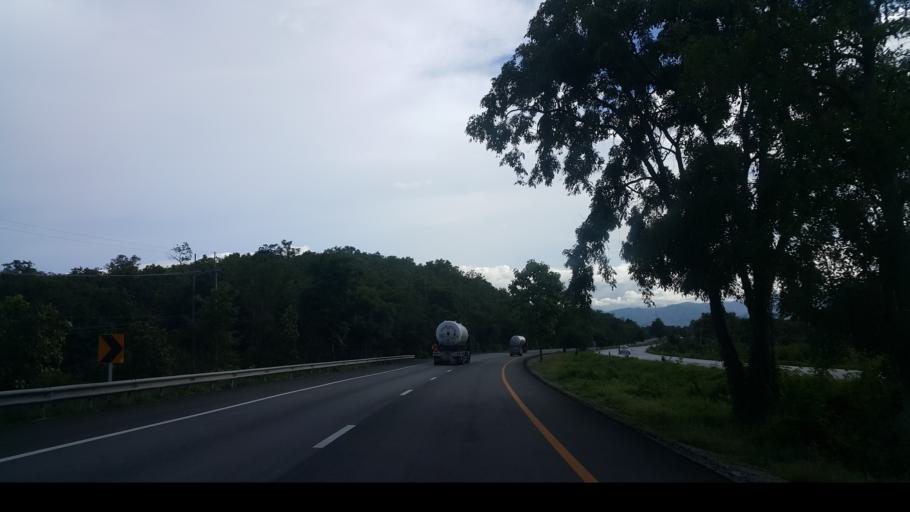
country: TH
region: Tak
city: Ban Tak
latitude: 17.1156
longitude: 99.0922
